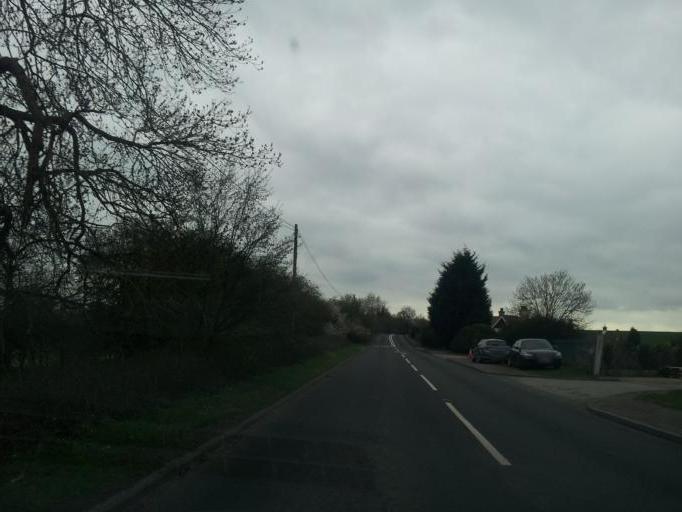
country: GB
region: England
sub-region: Hertfordshire
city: Great Munden
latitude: 51.8996
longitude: 0.0199
